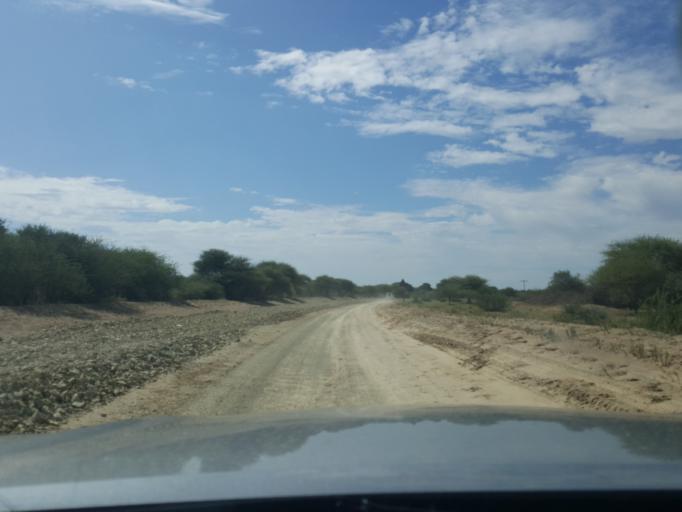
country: BW
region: Kweneng
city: Letlhakeng
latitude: -23.9803
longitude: 24.9668
